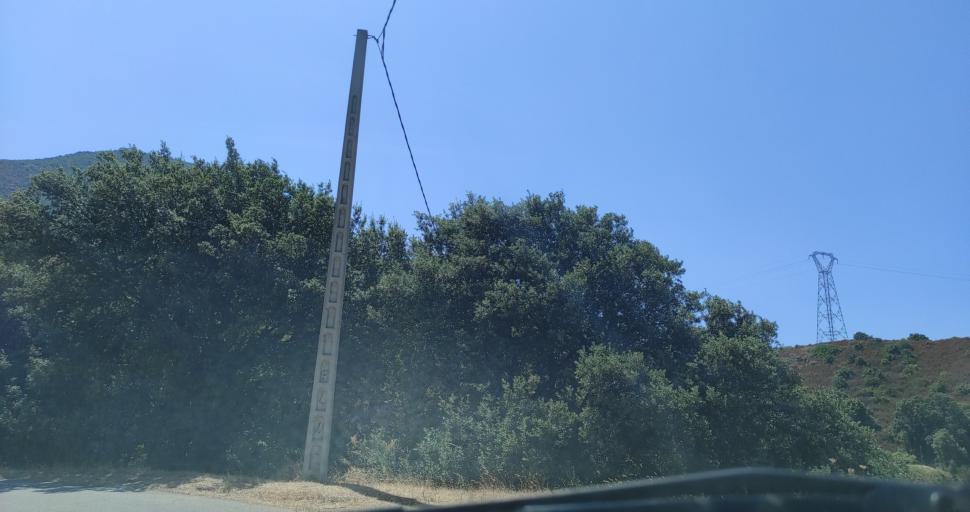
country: FR
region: Corsica
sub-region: Departement de la Corse-du-Sud
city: Alata
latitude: 41.9679
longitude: 8.7104
